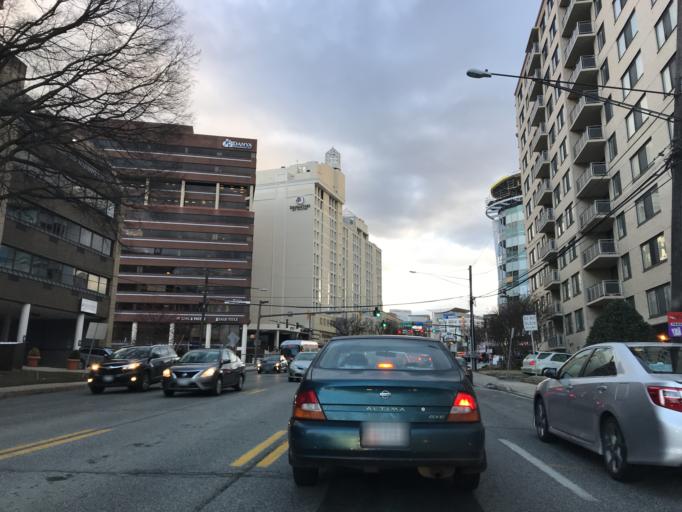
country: US
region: Maryland
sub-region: Montgomery County
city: Silver Spring
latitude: 38.9998
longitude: -77.0258
